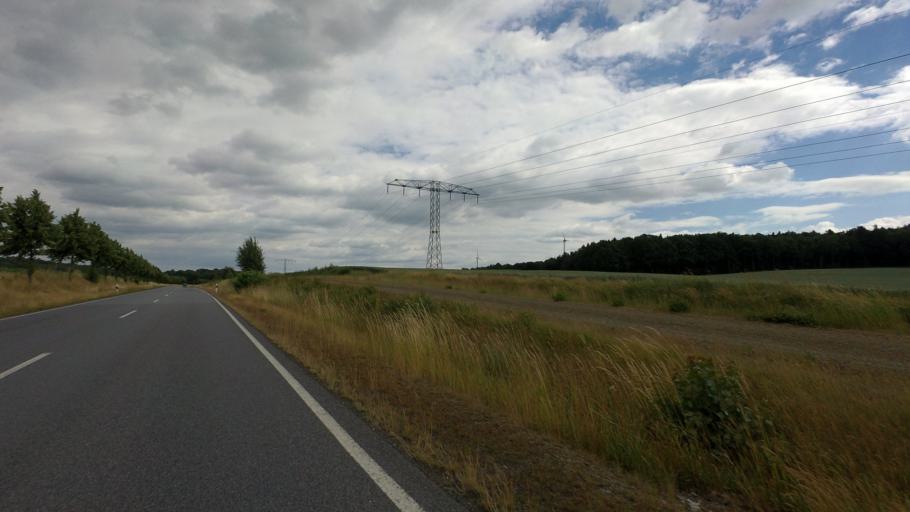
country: DE
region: Saxony
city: Nebelschutz
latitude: 51.2555
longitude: 14.1590
